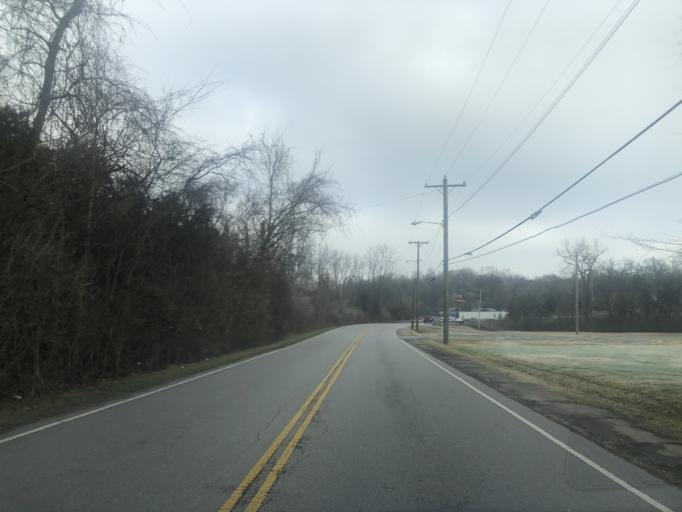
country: US
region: Tennessee
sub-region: Rutherford County
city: La Vergne
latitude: 36.0576
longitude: -86.6725
